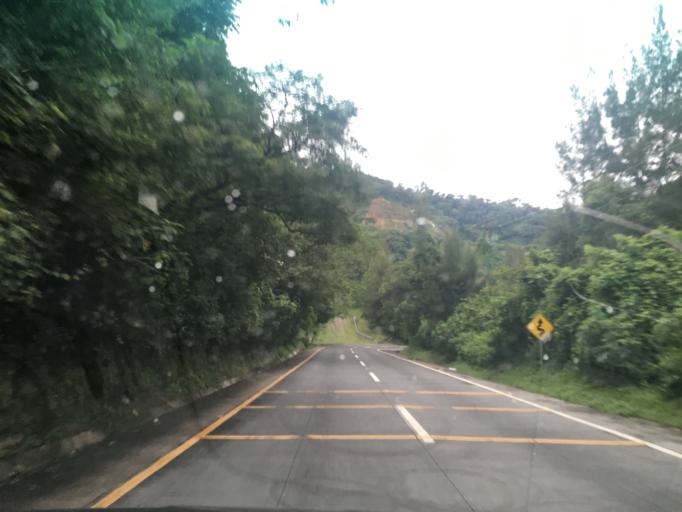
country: GT
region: Sacatepequez
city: Santa Lucia Milpas Altas
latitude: 14.5677
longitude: -90.6918
